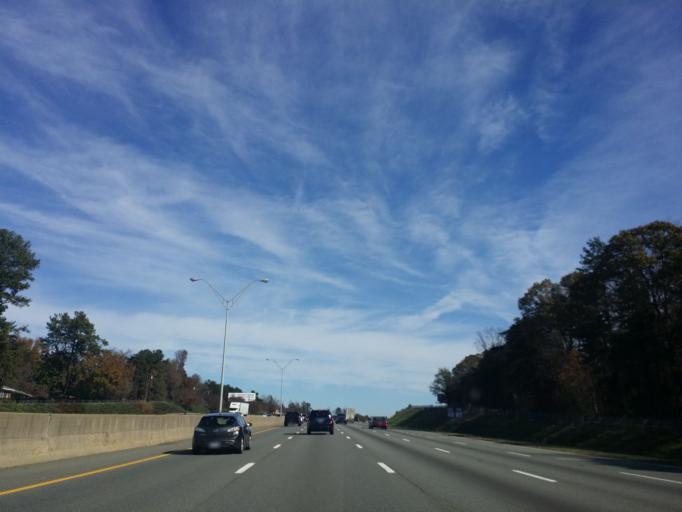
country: US
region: North Carolina
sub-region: Alamance County
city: Graham
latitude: 36.0658
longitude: -79.3796
